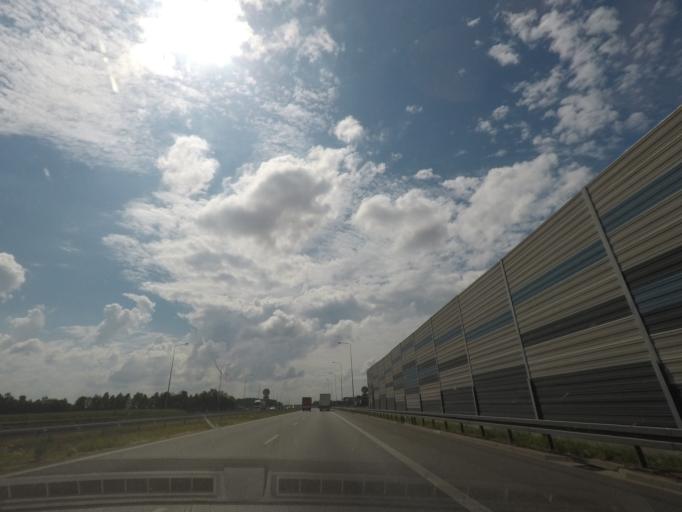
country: PL
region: Lodz Voivodeship
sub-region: Powiat leczycki
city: Piatek
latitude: 52.0137
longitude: 19.5427
